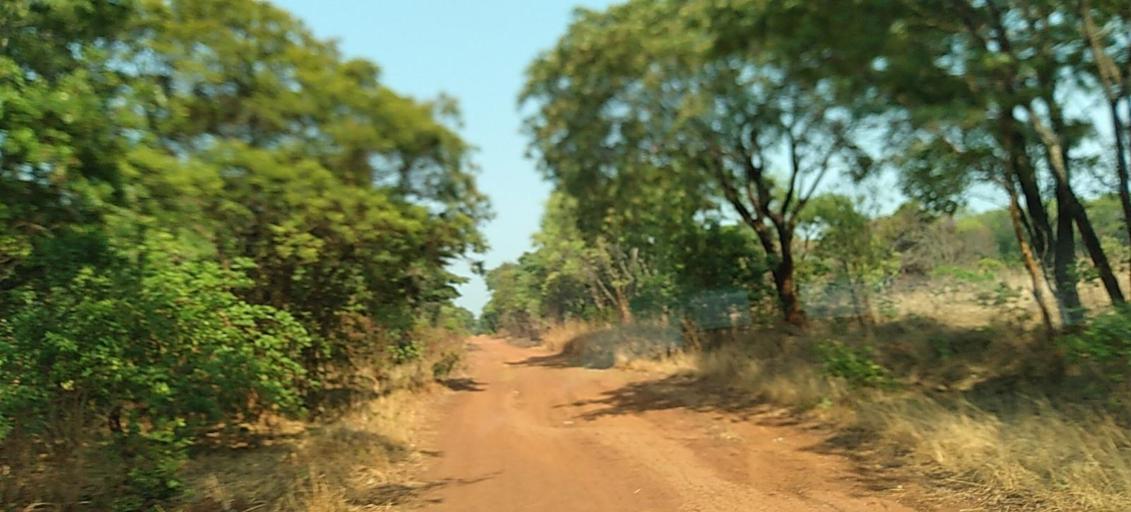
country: ZM
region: Copperbelt
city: Chingola
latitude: -12.8863
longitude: 27.4208
